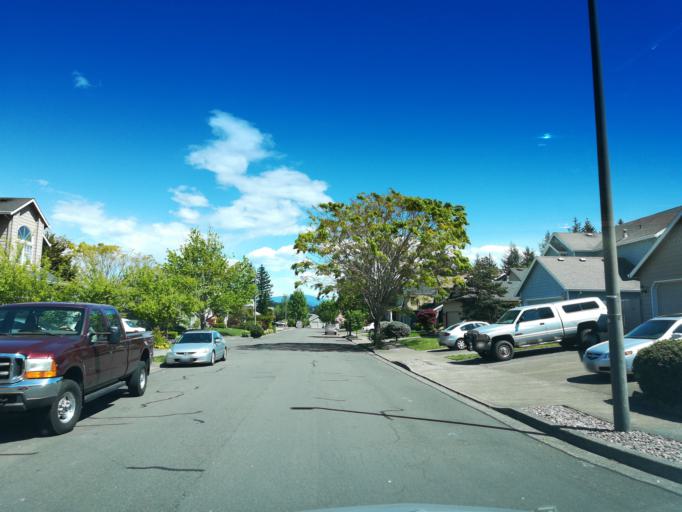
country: US
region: Oregon
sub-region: Multnomah County
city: Troutdale
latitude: 45.5233
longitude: -122.3945
